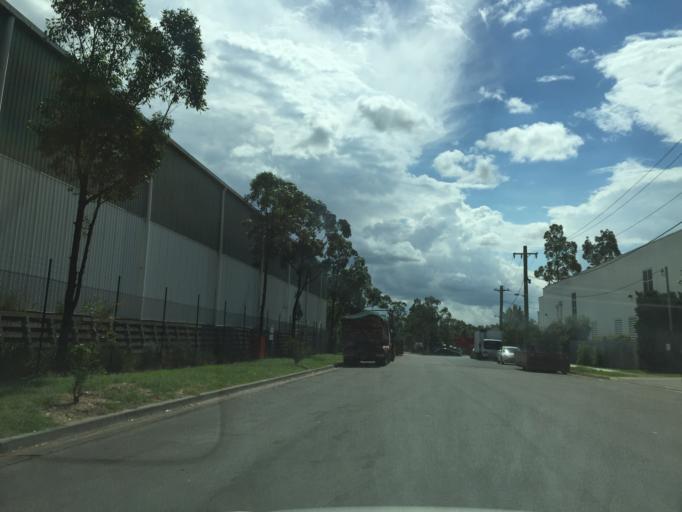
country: AU
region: New South Wales
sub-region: Blacktown
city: Doonside
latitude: -33.7902
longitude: 150.8742
